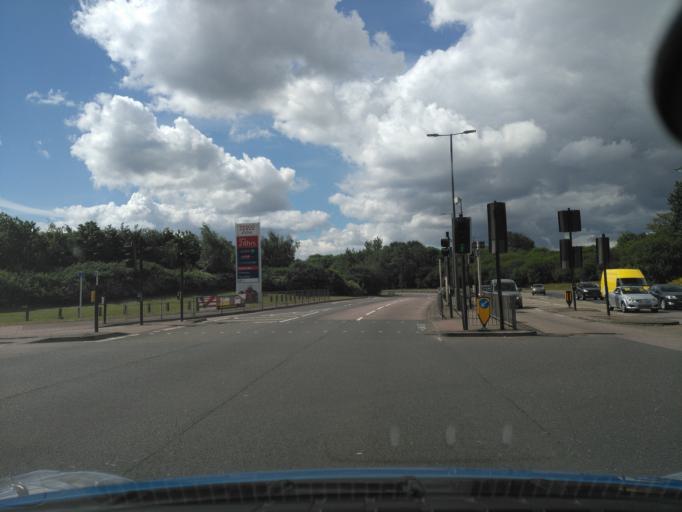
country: GB
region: England
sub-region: Greater London
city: Barking
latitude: 51.5153
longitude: 0.0717
